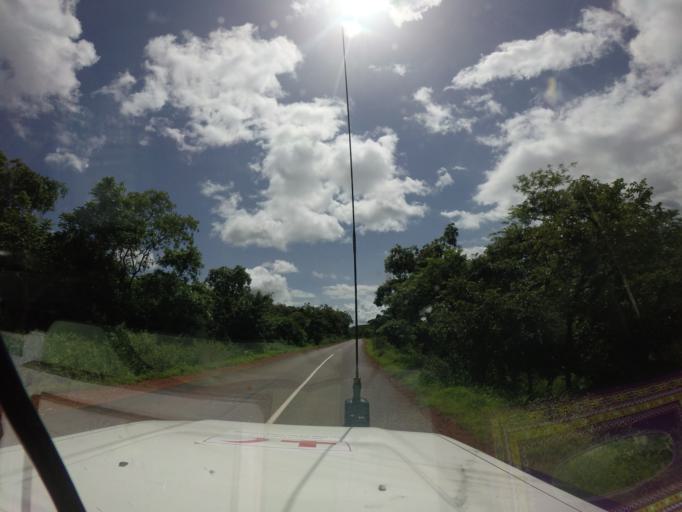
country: GN
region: Mamou
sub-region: Mamou Prefecture
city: Mamou
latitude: 10.1871
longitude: -11.7443
